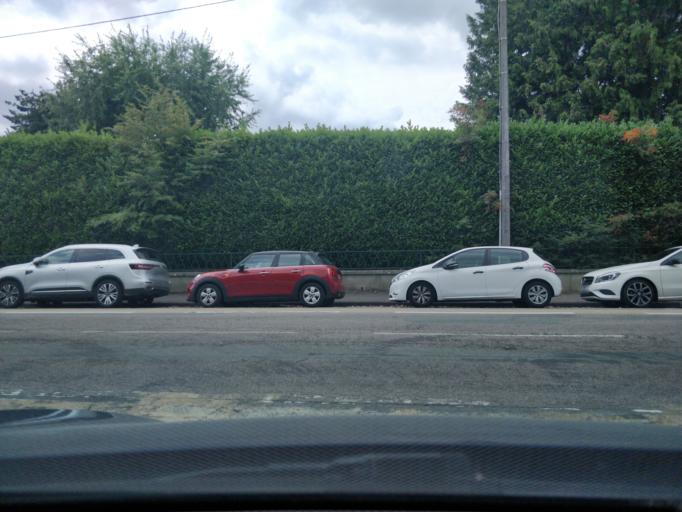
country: FR
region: Haute-Normandie
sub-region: Departement de la Seine-Maritime
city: Bois-Guillaume
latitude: 49.4751
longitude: 1.1127
